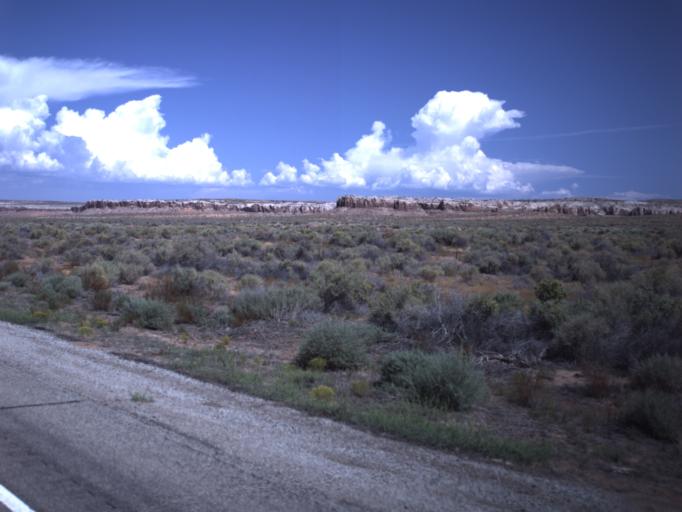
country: US
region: Utah
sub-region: San Juan County
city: Blanding
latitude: 37.1840
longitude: -109.5907
